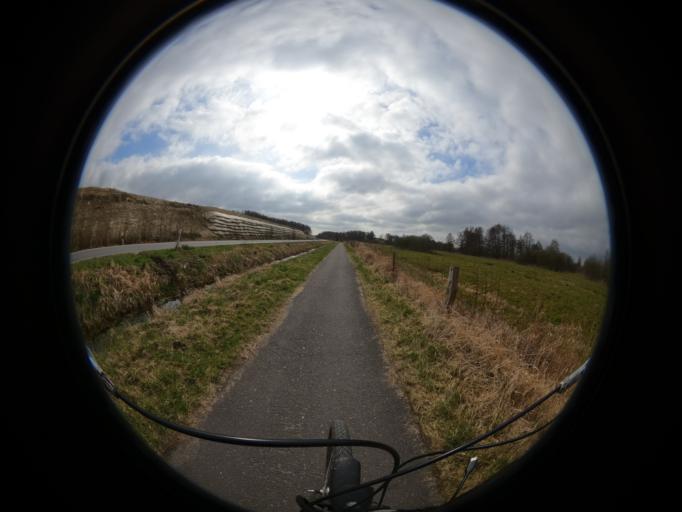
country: DE
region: Lower Saxony
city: Neu Wulmstorf
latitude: 53.4866
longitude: 9.7808
